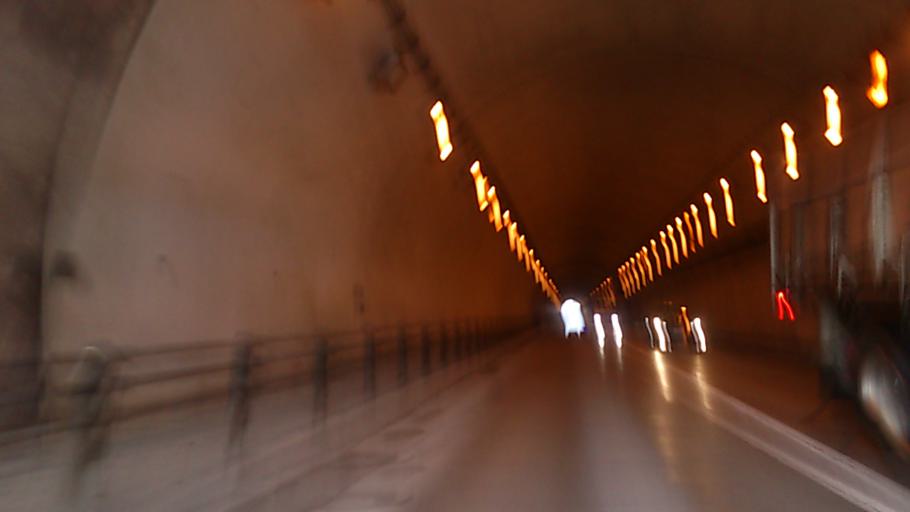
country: JP
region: Hokkaido
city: Iwanai
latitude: 42.8761
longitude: 140.3632
